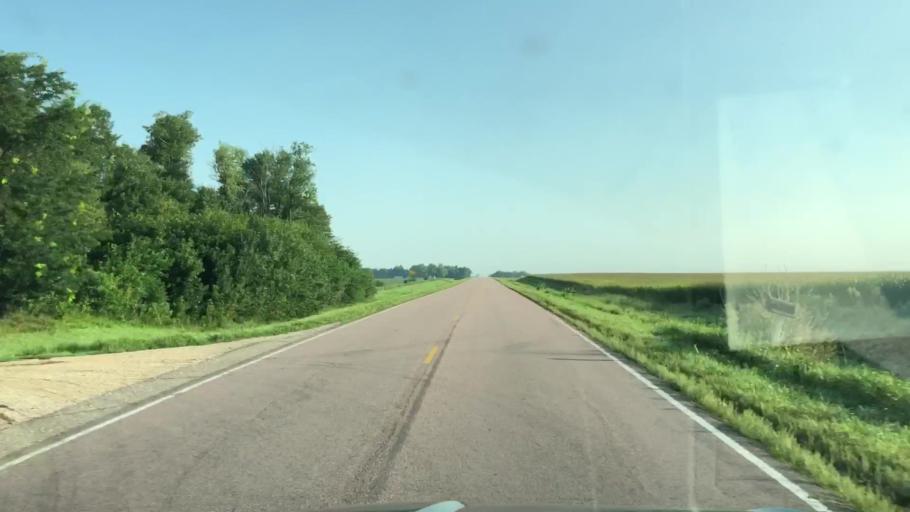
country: US
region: Iowa
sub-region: Lyon County
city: George
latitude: 43.2812
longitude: -95.9997
